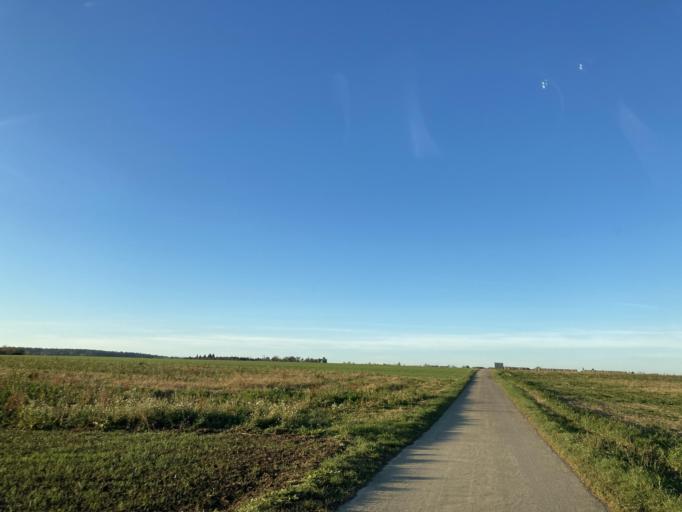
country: DE
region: Baden-Wuerttemberg
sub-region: Tuebingen Region
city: Hirrlingen
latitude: 48.4219
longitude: 8.8783
